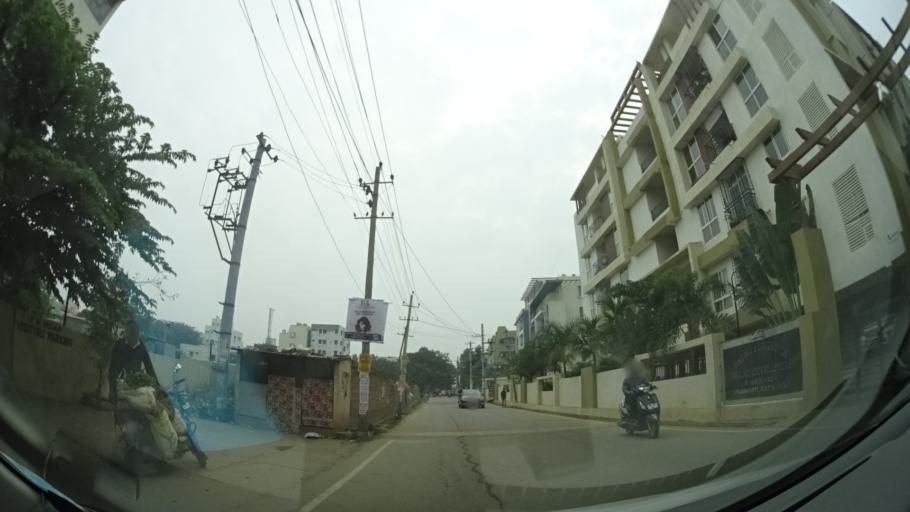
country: IN
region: Karnataka
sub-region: Bangalore Rural
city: Hoskote
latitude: 12.9833
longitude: 77.7457
